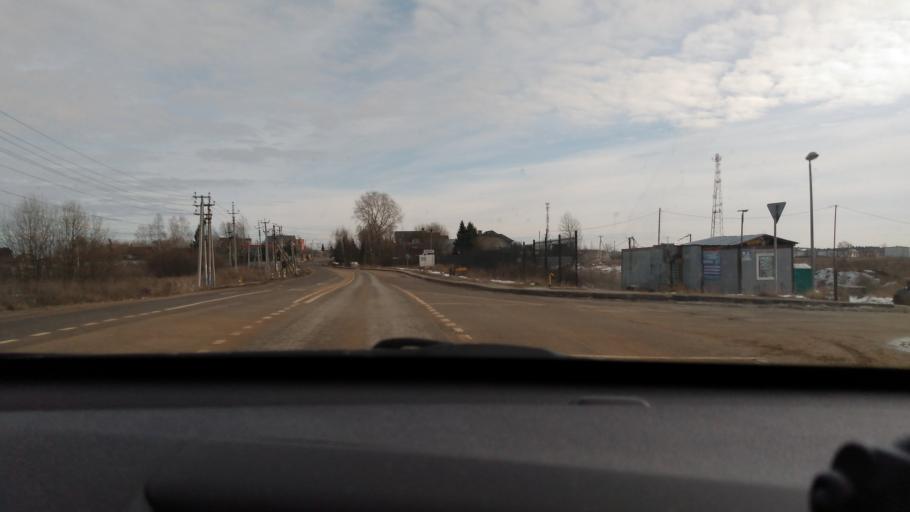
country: RU
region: Moskovskaya
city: Nakhabino
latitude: 55.8920
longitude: 37.1646
